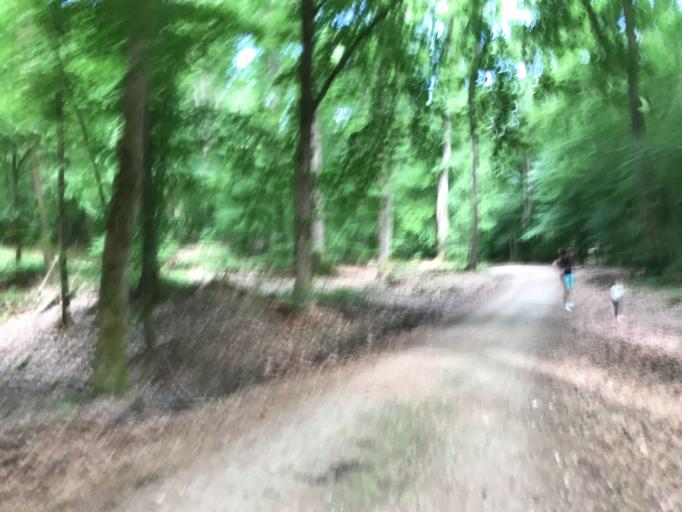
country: DE
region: Hesse
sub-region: Regierungsbezirk Darmstadt
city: Walluf
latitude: 50.0780
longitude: 8.1830
